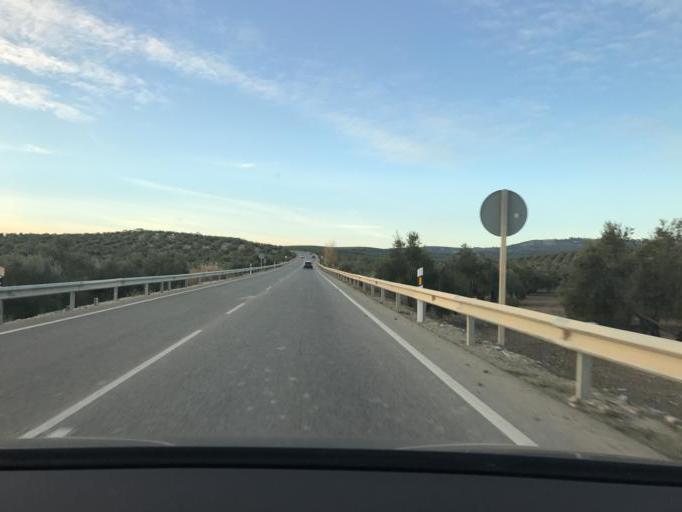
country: ES
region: Andalusia
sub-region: Provincia de Jaen
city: Ubeda
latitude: 37.9661
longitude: -3.3633
